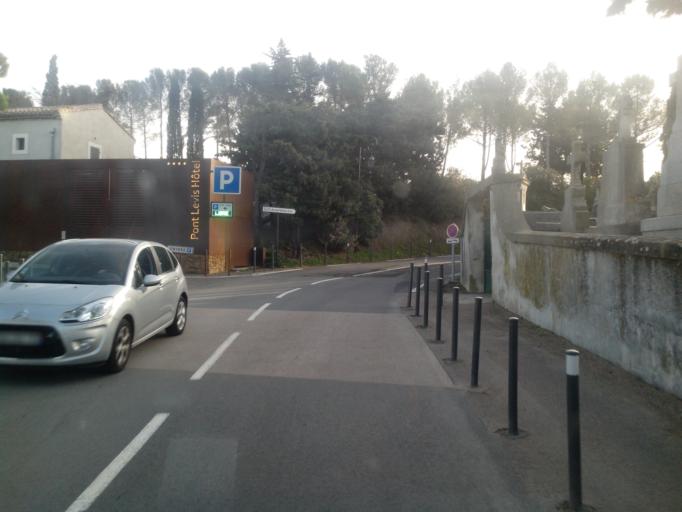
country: FR
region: Languedoc-Roussillon
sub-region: Departement de l'Aude
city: Carcassonne
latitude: 43.2060
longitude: 2.3667
